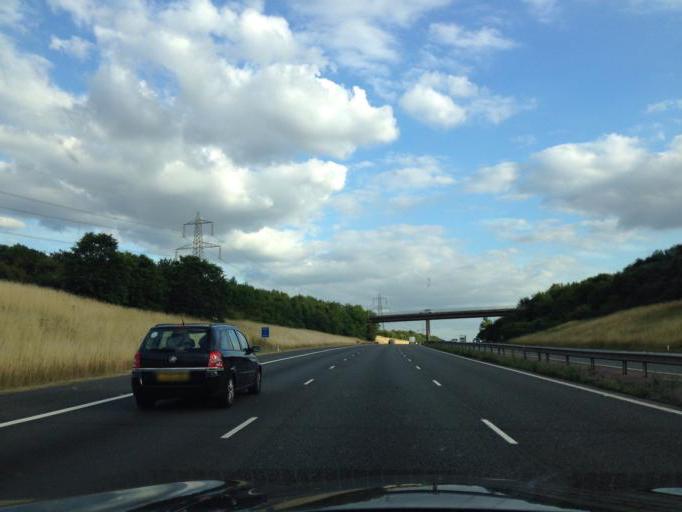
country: GB
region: England
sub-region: Oxfordshire
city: Wheatley
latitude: 51.8232
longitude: -1.1082
